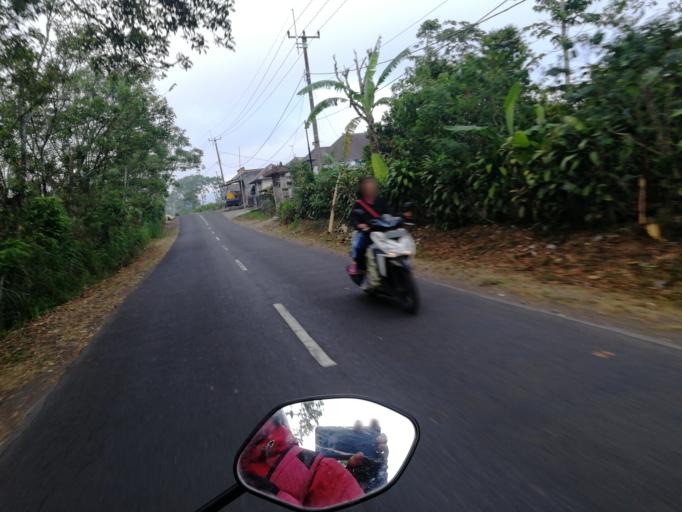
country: ID
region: Bali
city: Banjar Ambengan
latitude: -8.2308
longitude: 115.2436
